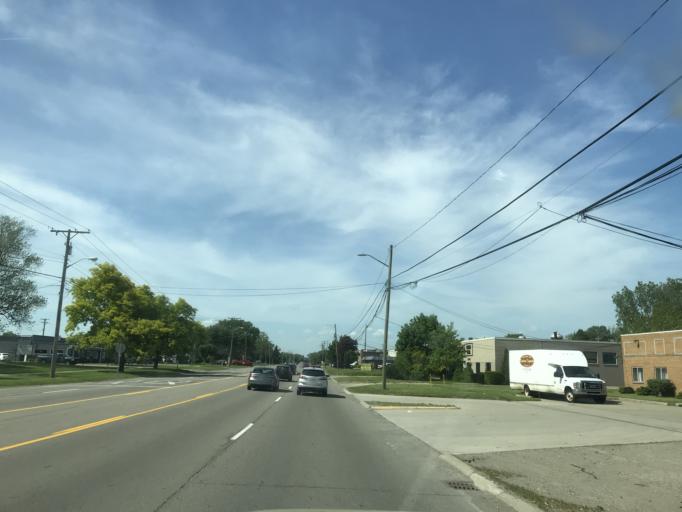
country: US
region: Michigan
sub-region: Wayne County
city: Redford
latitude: 42.3778
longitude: -83.3138
